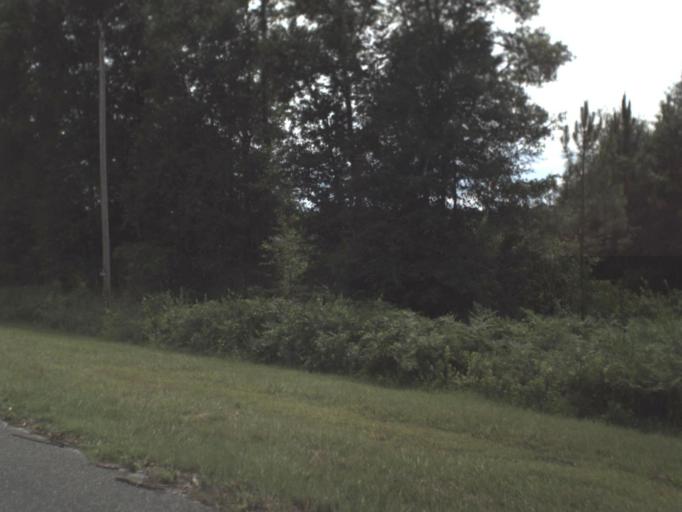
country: US
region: Florida
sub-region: Taylor County
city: Perry
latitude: 30.0849
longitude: -83.4992
